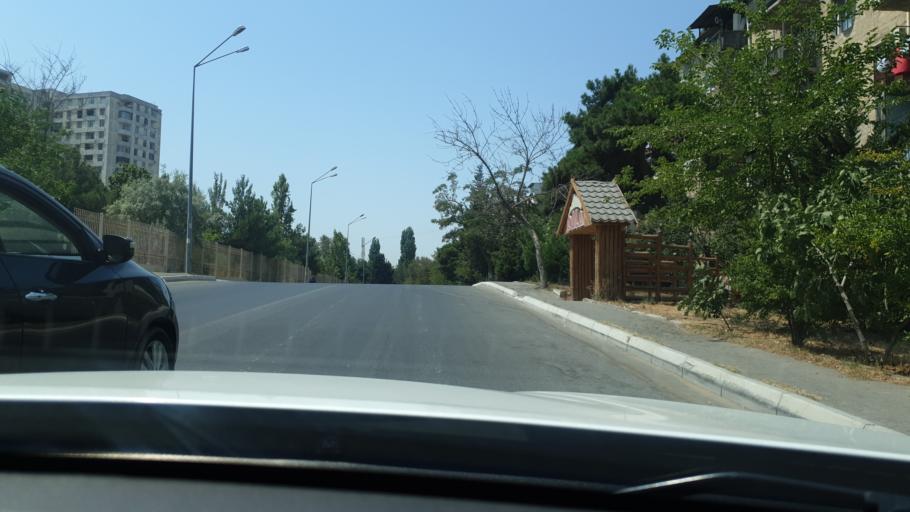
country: AZ
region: Baki
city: Bakixanov
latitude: 40.4162
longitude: 49.9460
